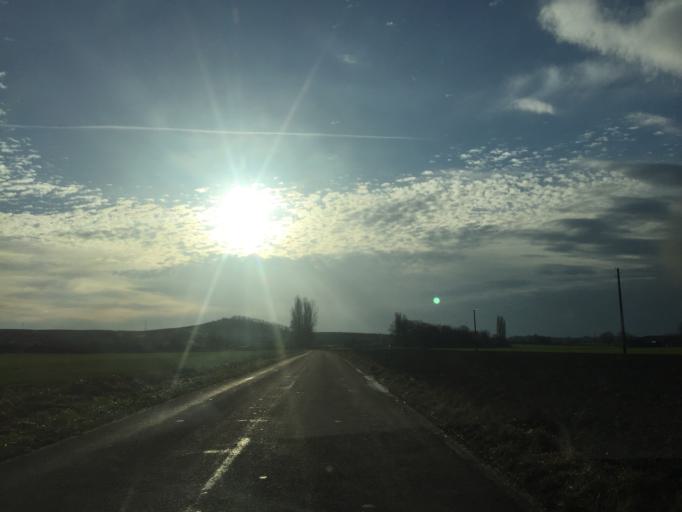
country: FR
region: Franche-Comte
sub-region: Departement du Jura
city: Arbois
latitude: 46.9203
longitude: 5.7482
